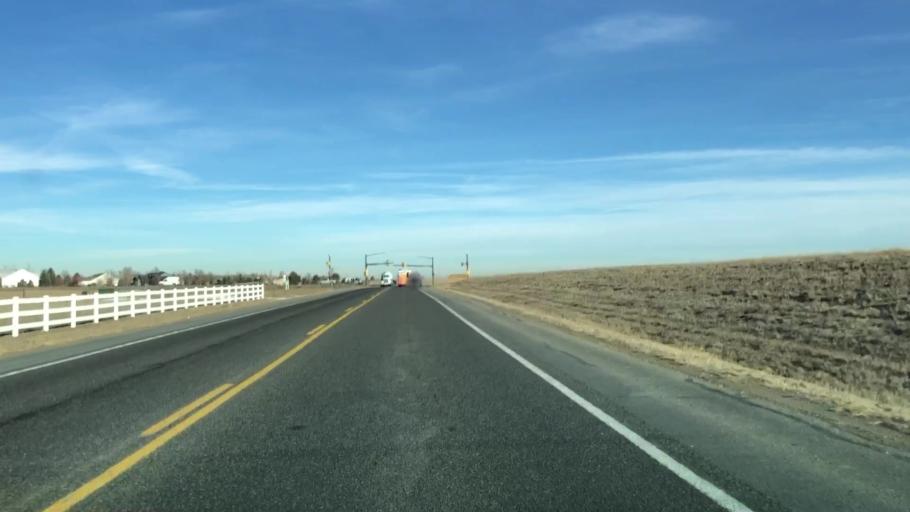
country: US
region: Colorado
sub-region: Weld County
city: Windsor
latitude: 40.4340
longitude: -104.9442
